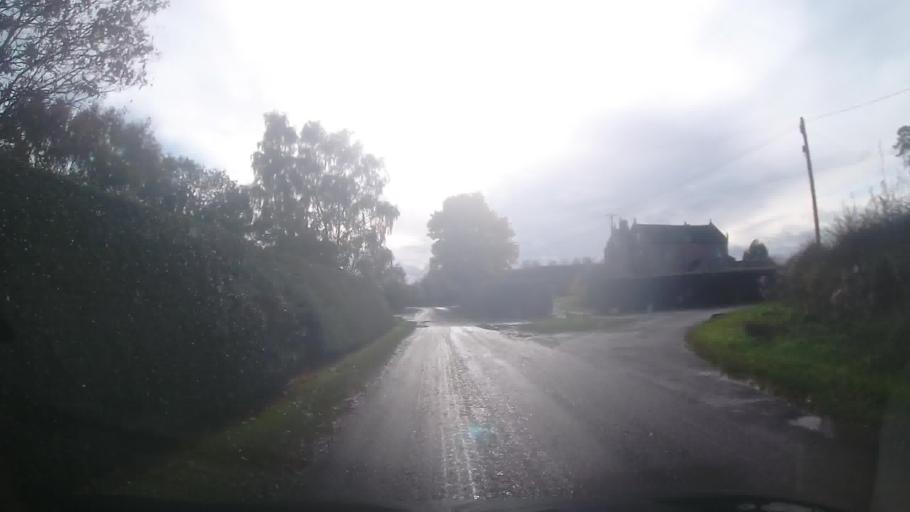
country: GB
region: England
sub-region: Shropshire
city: Whitchurch
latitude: 52.9494
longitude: -2.6993
